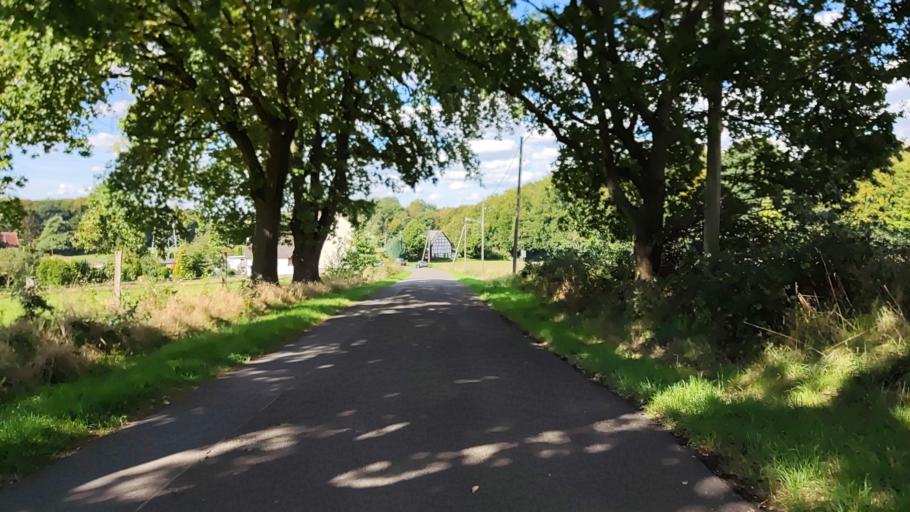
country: DE
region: North Rhine-Westphalia
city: Witten
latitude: 51.4526
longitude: 7.3078
